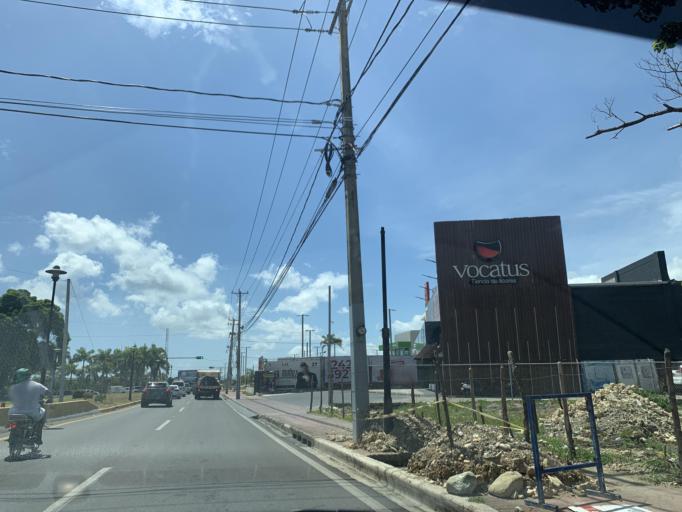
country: DO
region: Puerto Plata
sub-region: Puerto Plata
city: Puerto Plata
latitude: 19.7829
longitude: -70.6749
